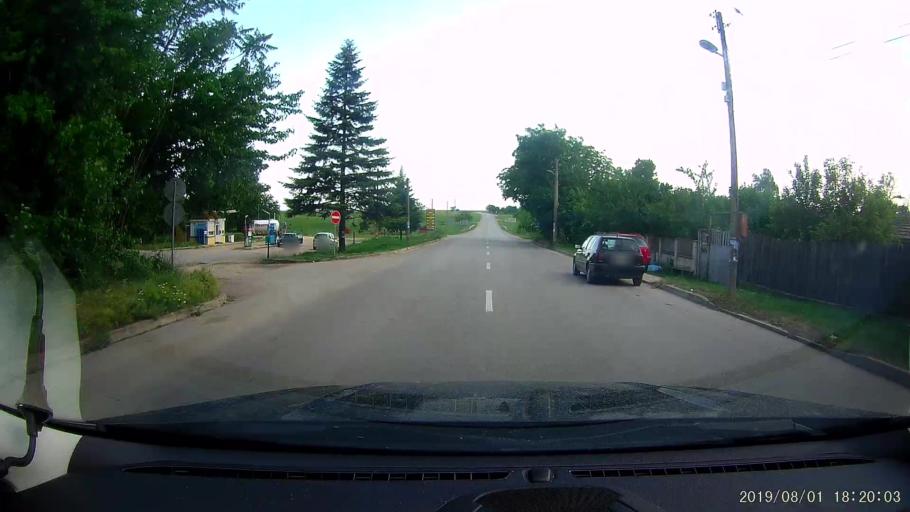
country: BG
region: Shumen
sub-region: Obshtina Kaolinovo
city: Kaolinovo
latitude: 43.6783
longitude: 27.0904
